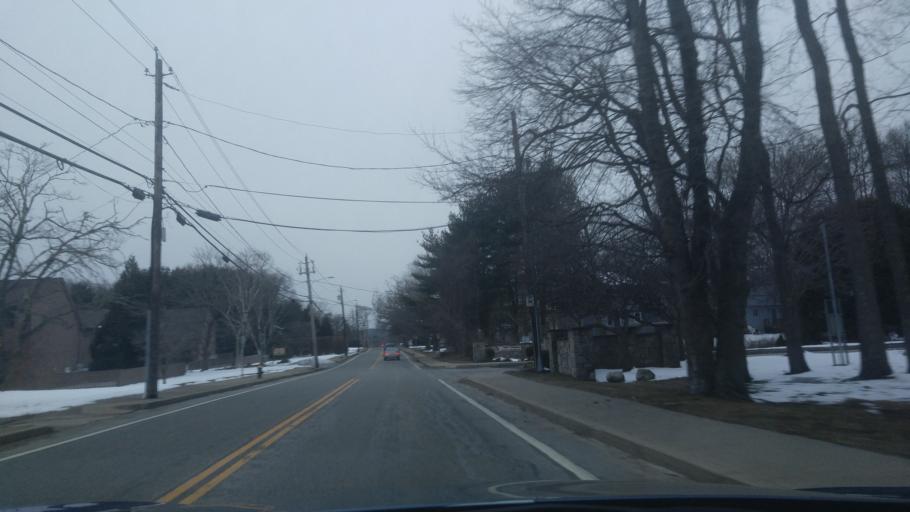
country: US
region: Rhode Island
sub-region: Providence County
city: Cranston
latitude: 41.7344
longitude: -71.4720
